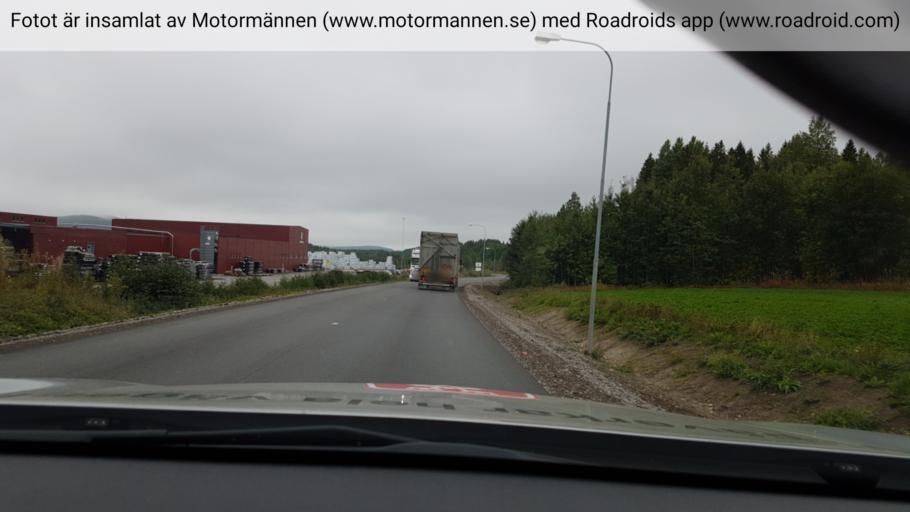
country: SE
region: Vaesterbotten
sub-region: Skelleftea Kommun
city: Burtraesk
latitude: 64.3604
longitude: 20.5037
